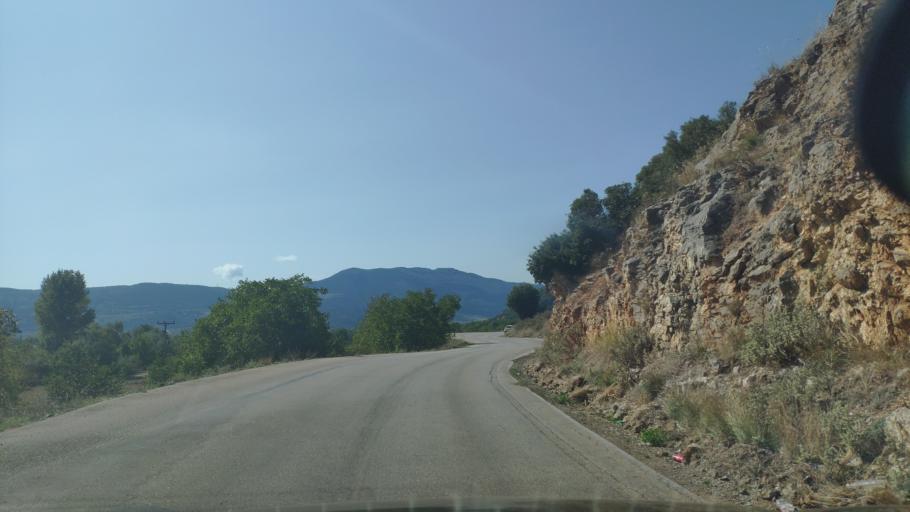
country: GR
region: Peloponnese
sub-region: Nomos Korinthias
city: Nemea
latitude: 37.9140
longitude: 22.5274
